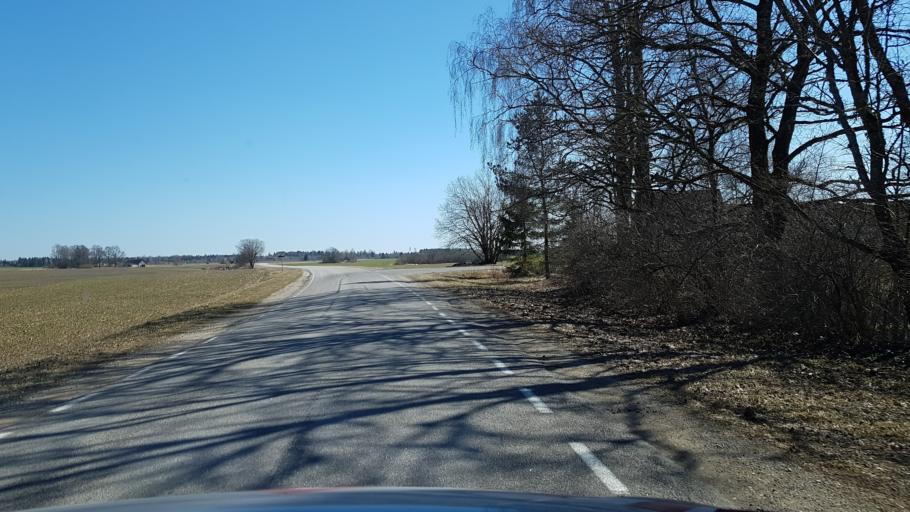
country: EE
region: Laeaene-Virumaa
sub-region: Vaeike-Maarja vald
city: Vaike-Maarja
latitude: 59.1084
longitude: 26.3785
